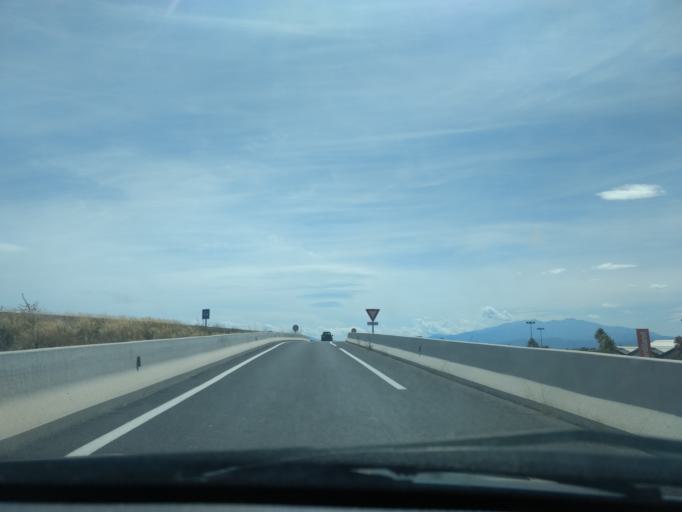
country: FR
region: Languedoc-Roussillon
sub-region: Departement des Pyrenees-Orientales
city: Cabestany
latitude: 42.6649
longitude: 2.9174
